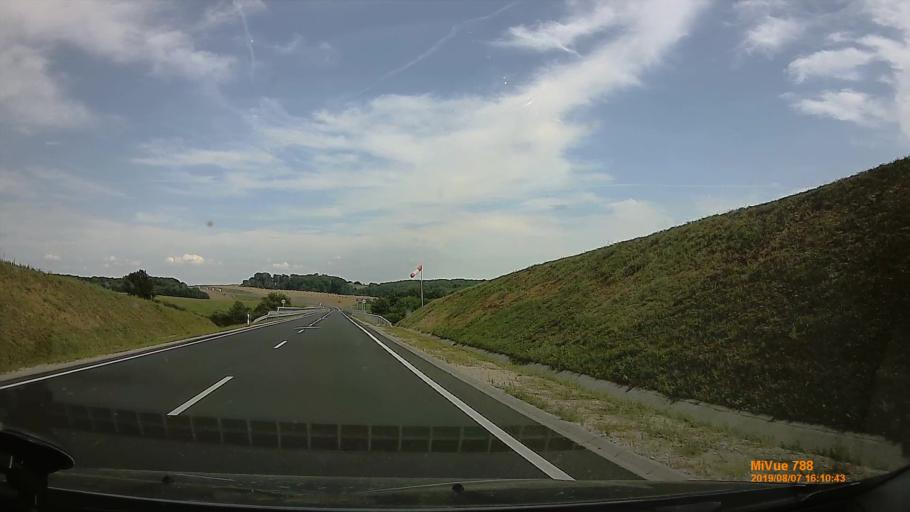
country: HU
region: Zala
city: Zalalovo
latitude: 46.8753
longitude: 16.6062
